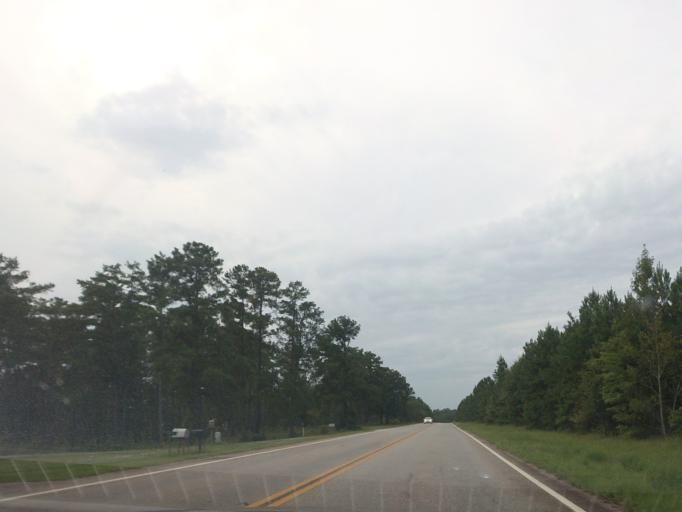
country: US
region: Georgia
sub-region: Twiggs County
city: Jeffersonville
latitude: 32.7039
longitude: -83.3791
